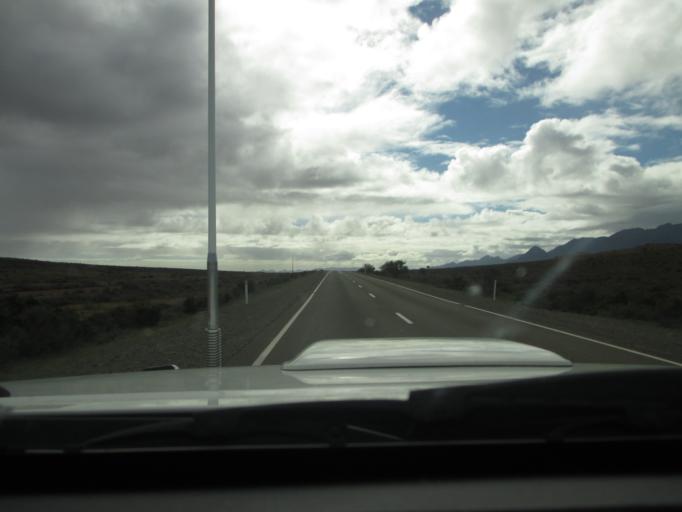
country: AU
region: South Australia
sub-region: Flinders Ranges
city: Quorn
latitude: -31.5776
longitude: 138.4201
